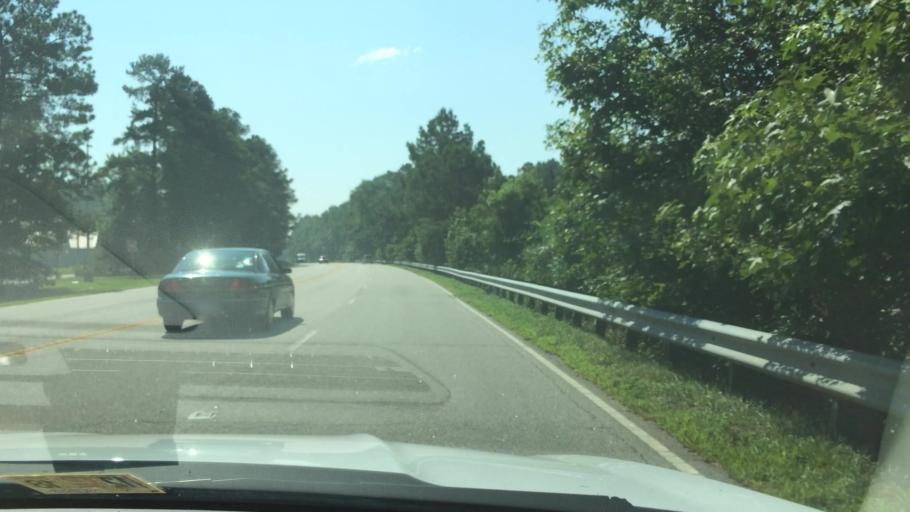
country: US
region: Virginia
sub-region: York County
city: Yorktown
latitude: 37.2168
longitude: -76.6058
